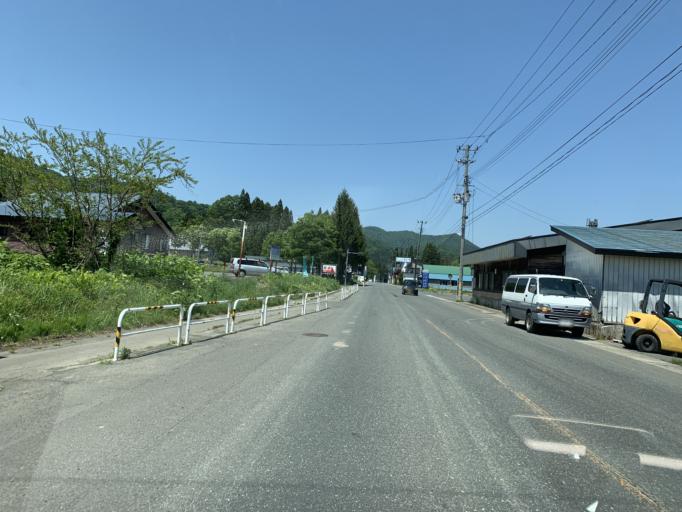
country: JP
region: Akita
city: Yokotemachi
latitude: 39.4330
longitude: 140.7510
